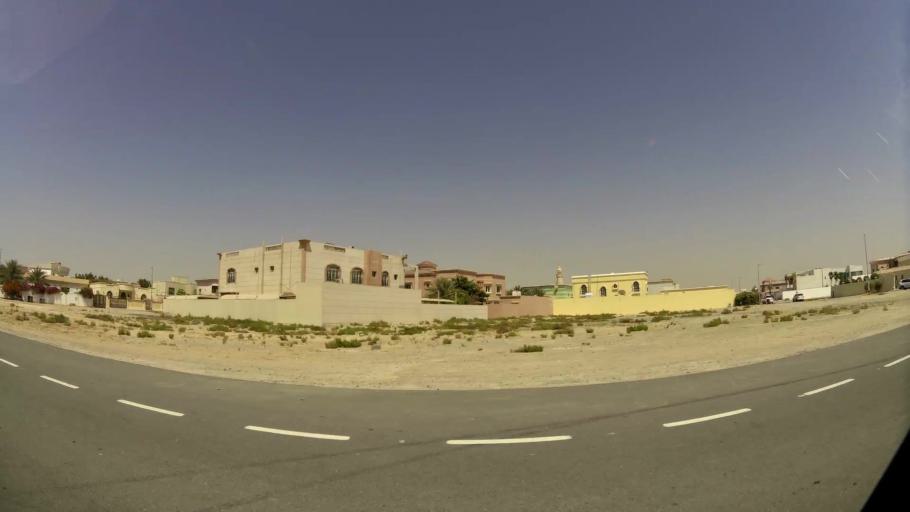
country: AE
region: Dubai
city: Dubai
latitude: 25.1085
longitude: 55.2064
